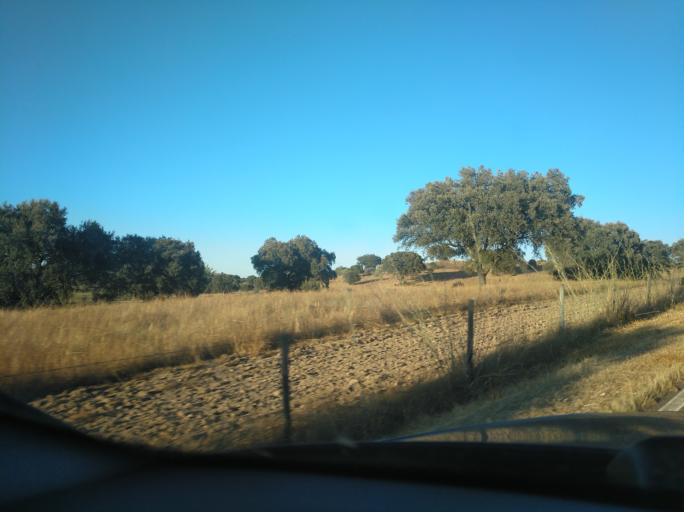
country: PT
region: Portalegre
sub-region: Arronches
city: Arronches
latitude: 39.0700
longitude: -7.2369
